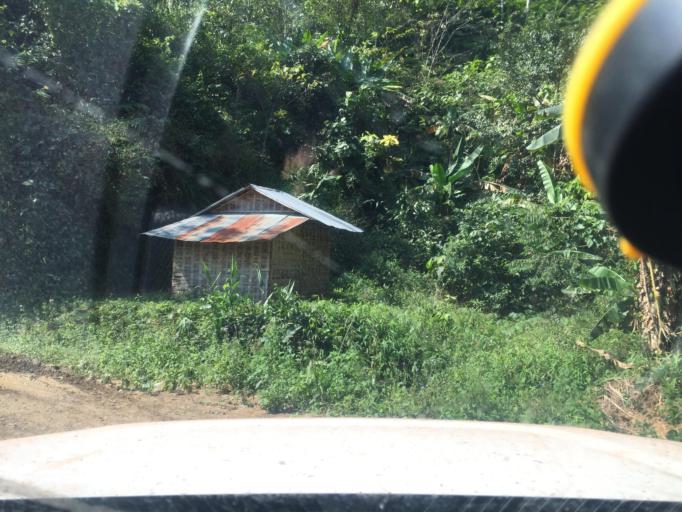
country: LA
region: Phongsali
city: Phongsali
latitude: 21.6572
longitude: 102.4145
